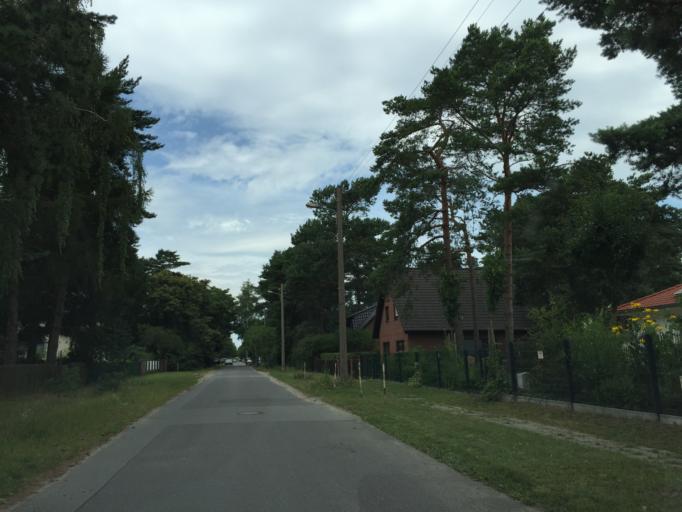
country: DE
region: Berlin
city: Mahlsdorf
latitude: 52.4879
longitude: 13.6223
